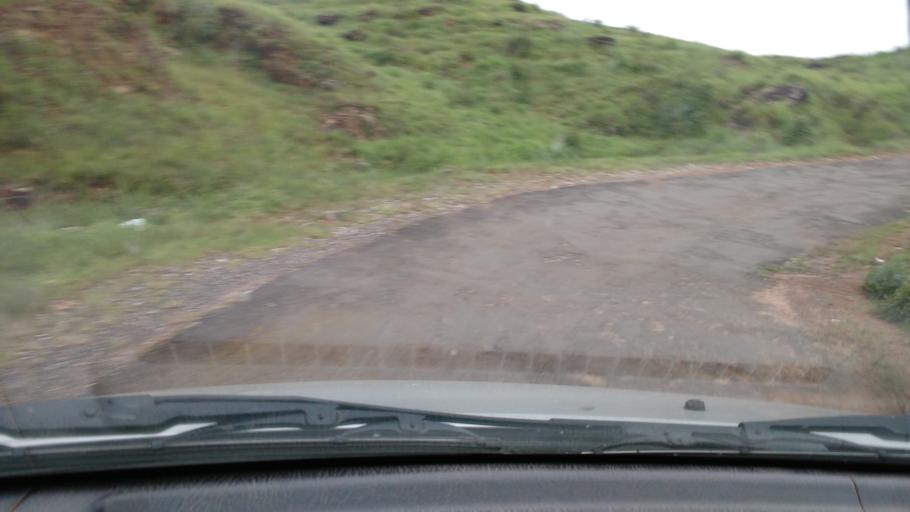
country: IN
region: Meghalaya
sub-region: East Khasi Hills
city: Cherrapunji
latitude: 25.2806
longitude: 91.6979
